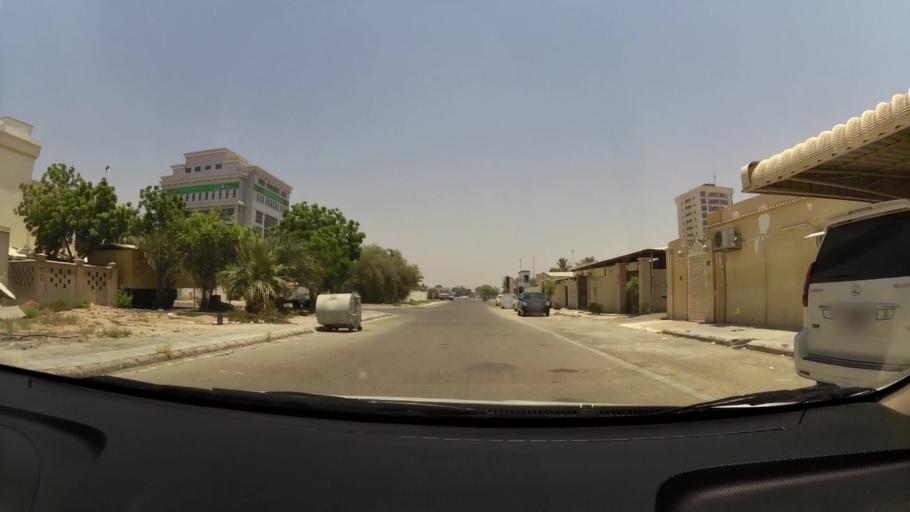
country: AE
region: Umm al Qaywayn
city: Umm al Qaywayn
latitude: 25.5524
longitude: 55.5454
